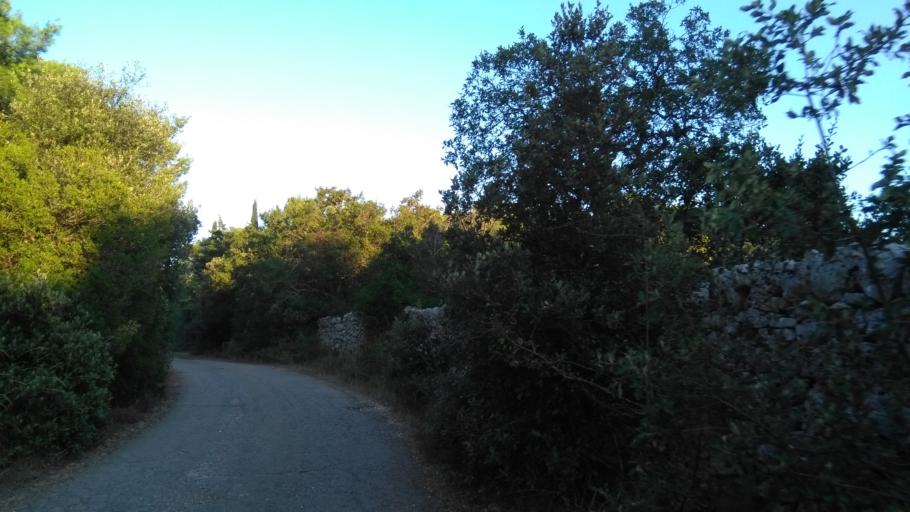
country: IT
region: Apulia
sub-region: Provincia di Bari
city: Putignano
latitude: 40.8248
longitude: 17.0804
